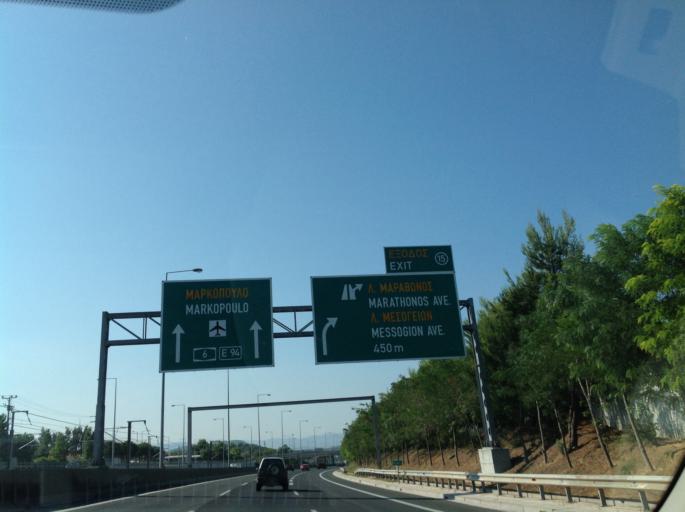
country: GR
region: Attica
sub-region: Nomarchia Anatolikis Attikis
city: Gerakas
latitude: 38.0142
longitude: 23.8671
